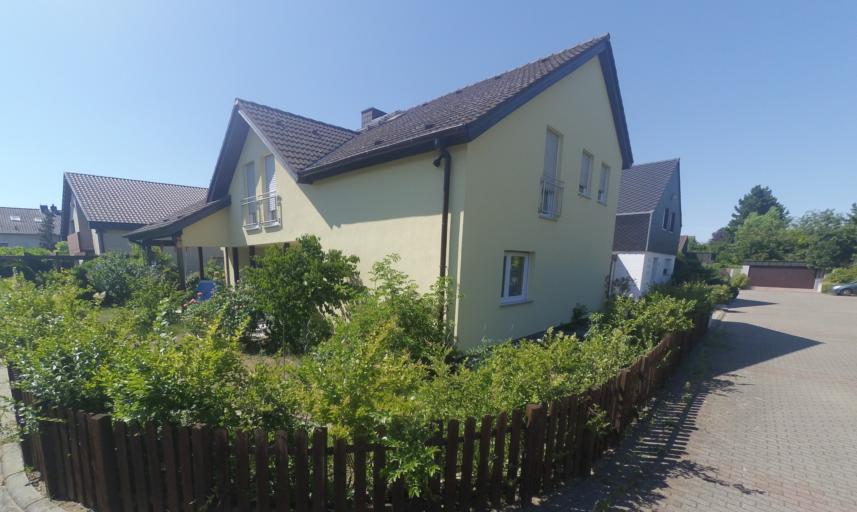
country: DE
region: Rheinland-Pfalz
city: Limburgerhof
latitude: 49.4233
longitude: 8.4020
